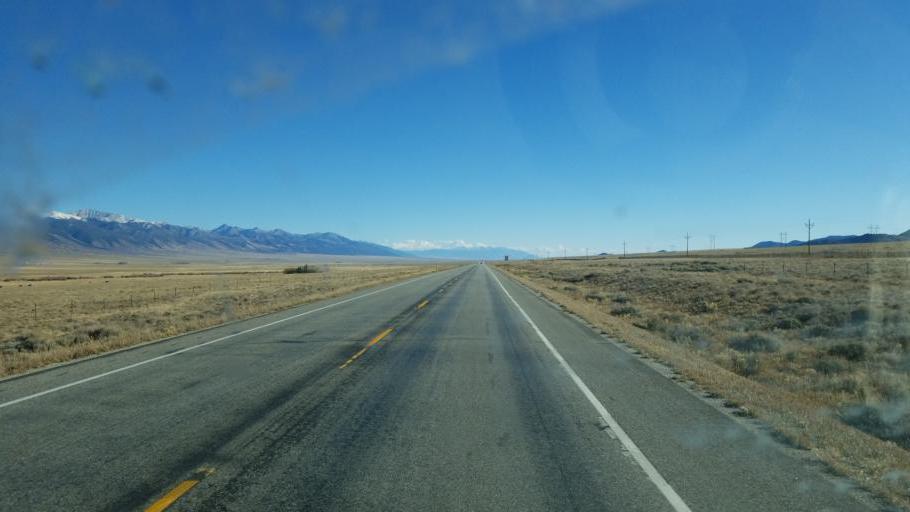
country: US
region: Colorado
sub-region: Chaffee County
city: Salida
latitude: 38.3481
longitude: -106.0234
